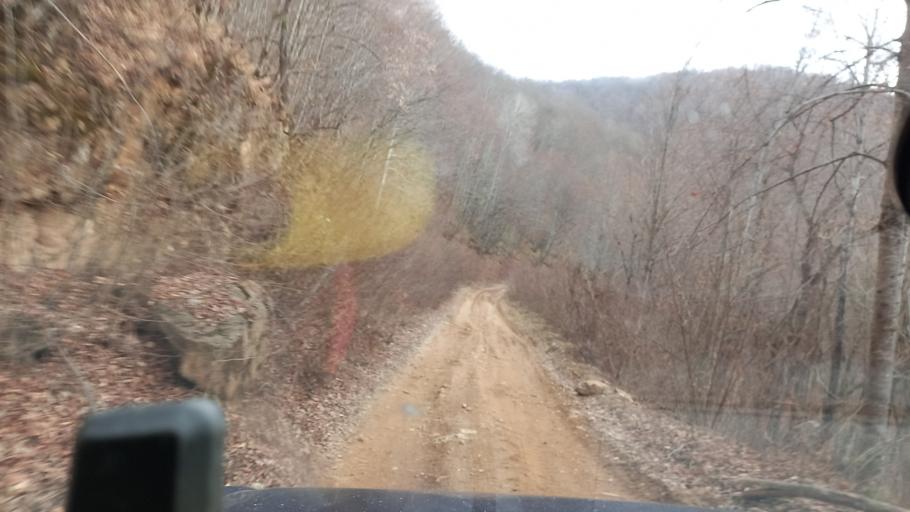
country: RU
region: Adygeya
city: Kamennomostskiy
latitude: 44.1772
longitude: 40.2983
